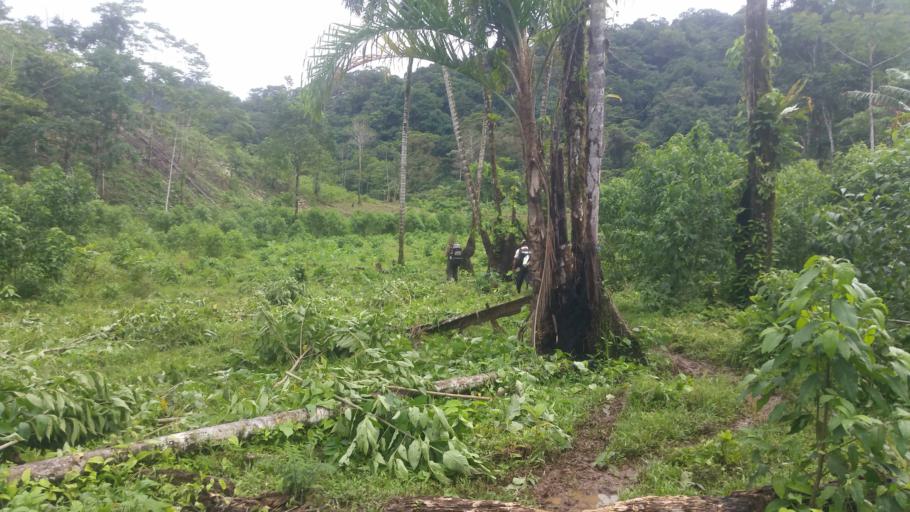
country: NI
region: Atlantico Norte (RAAN)
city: Bonanza
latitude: 14.0274
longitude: -84.7250
